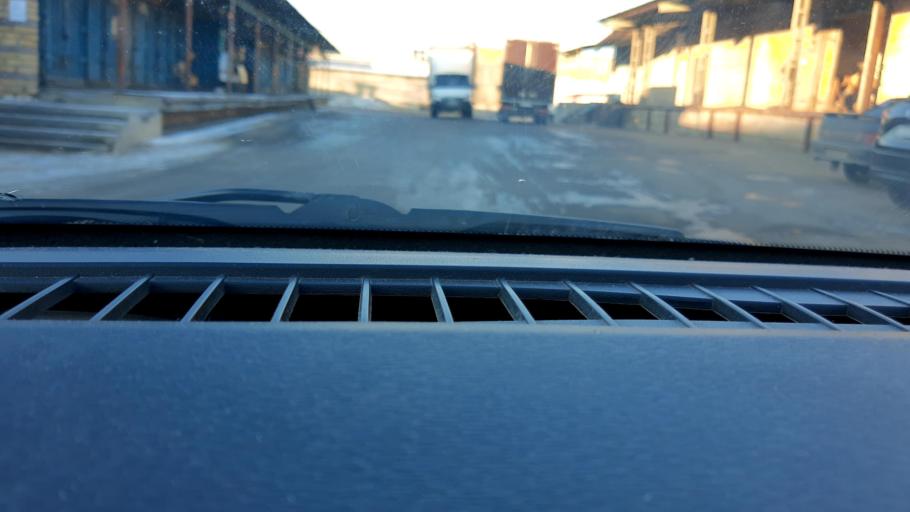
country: RU
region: Nizjnij Novgorod
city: Nizhniy Novgorod
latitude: 56.2593
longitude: 43.9196
